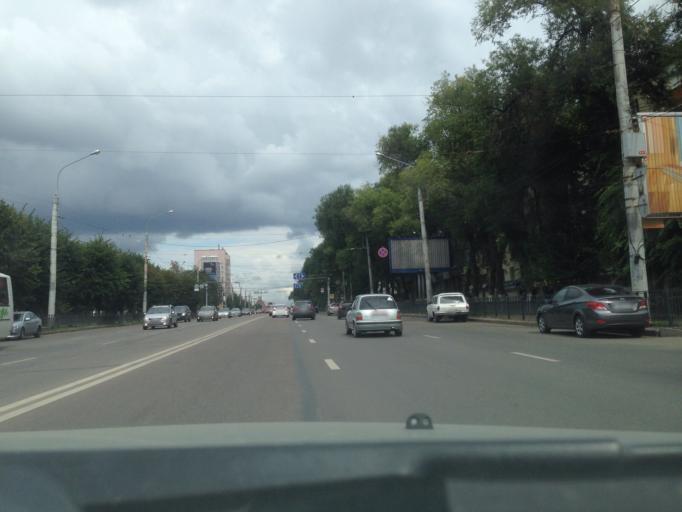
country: RU
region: Voronezj
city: Voronezh
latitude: 51.6968
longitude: 39.1827
